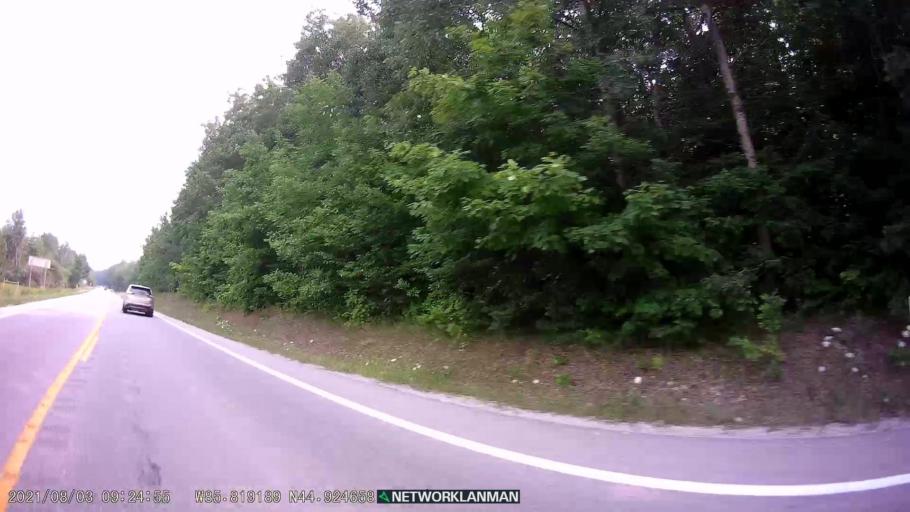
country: US
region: Michigan
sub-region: Leelanau County
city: Leland
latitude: 44.9250
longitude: -85.8190
